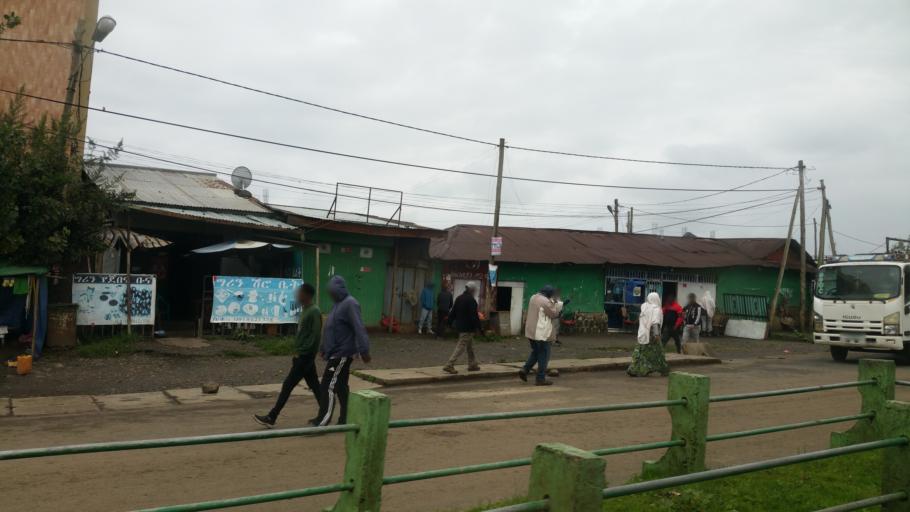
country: ET
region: Amhara
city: Debark'
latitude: 13.1576
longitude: 37.8983
